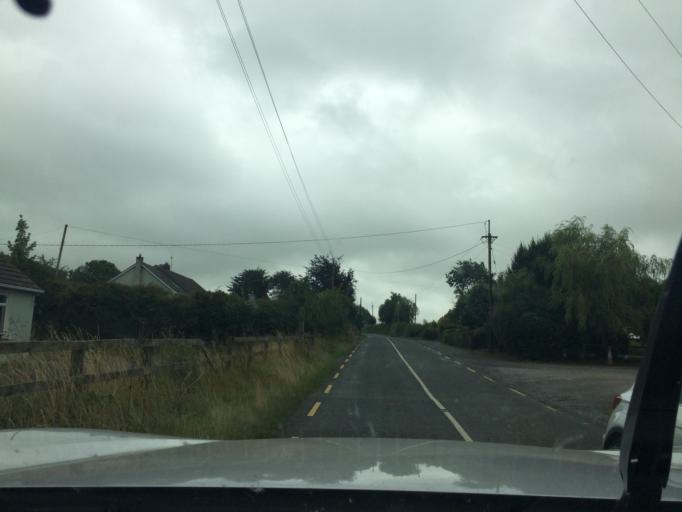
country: IE
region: Munster
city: Cashel
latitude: 52.5421
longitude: -7.8931
